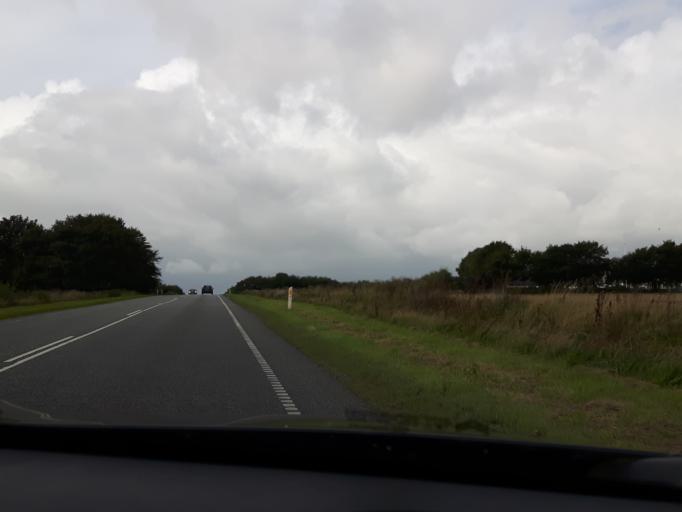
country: DK
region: North Denmark
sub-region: Jammerbugt Kommune
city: Brovst
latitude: 57.0938
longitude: 9.4608
